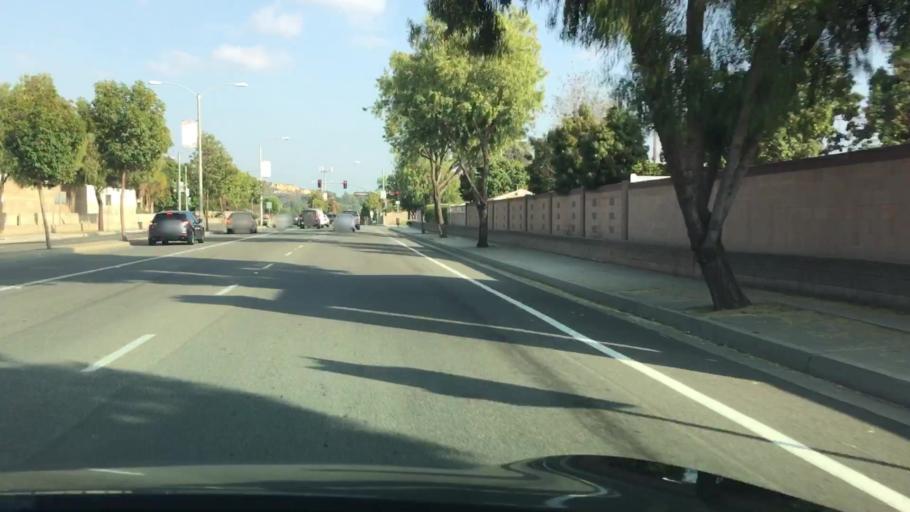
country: US
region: California
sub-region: Los Angeles County
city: La Mirada
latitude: 33.8989
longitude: -117.9980
